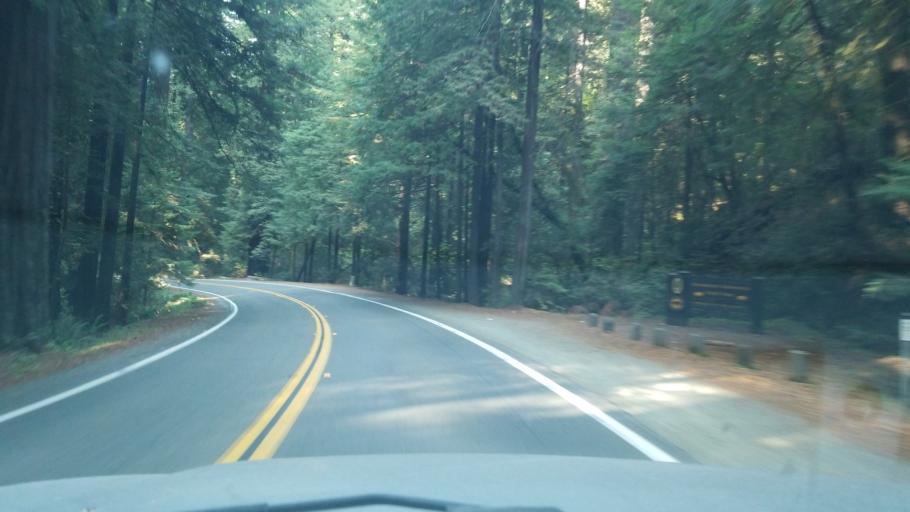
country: US
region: California
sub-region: Humboldt County
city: Redway
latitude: 40.2421
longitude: -123.8208
